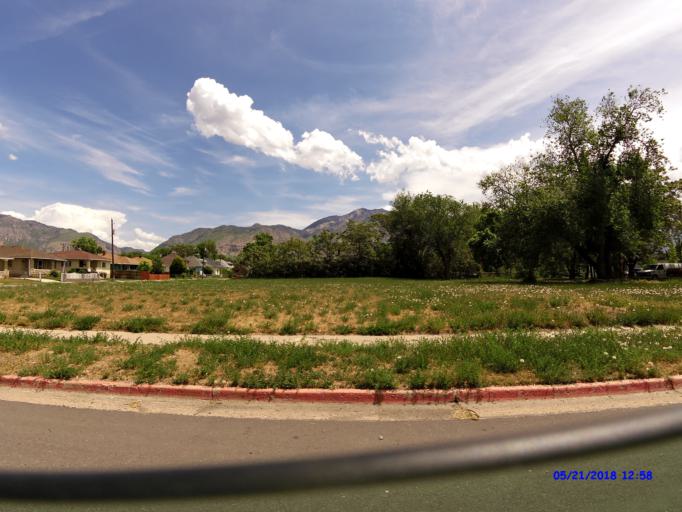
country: US
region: Utah
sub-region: Weber County
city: Ogden
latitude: 41.2089
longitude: -111.9763
